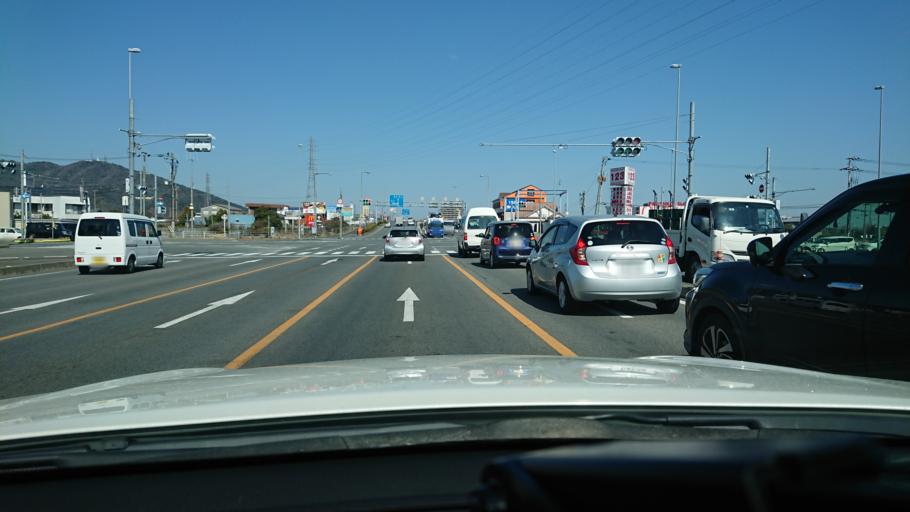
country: JP
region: Tokushima
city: Tokushima-shi
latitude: 34.0423
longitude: 134.5520
